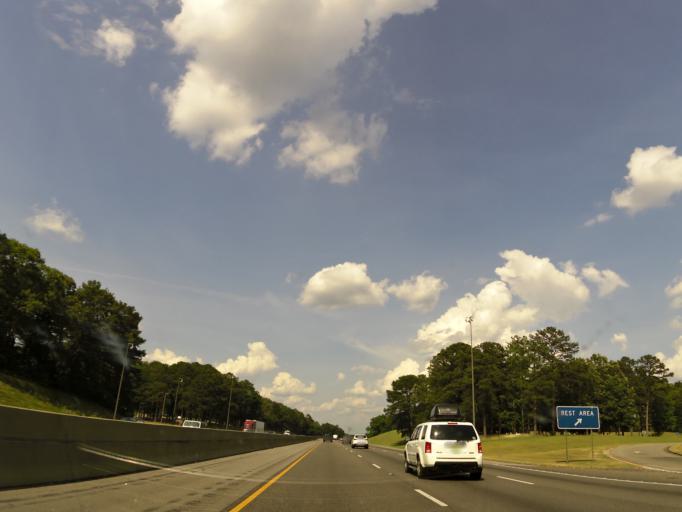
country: US
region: Alabama
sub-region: Tuscaloosa County
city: Coaling
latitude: 33.1885
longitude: -87.3281
